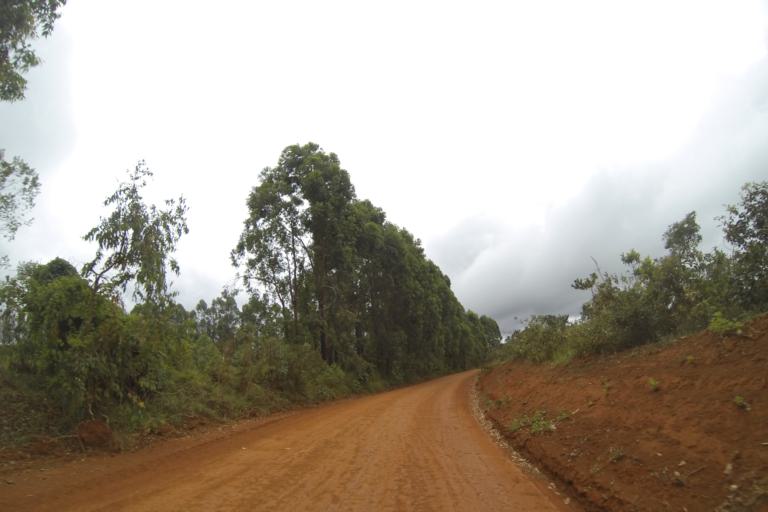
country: BR
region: Minas Gerais
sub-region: Campos Altos
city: Campos Altos
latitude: -19.8495
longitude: -46.3239
